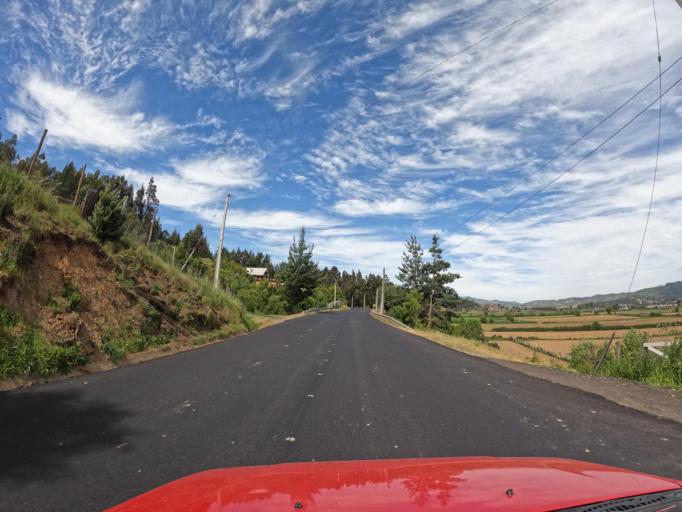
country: CL
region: Maule
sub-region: Provincia de Talca
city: Constitucion
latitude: -35.0786
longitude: -72.0328
